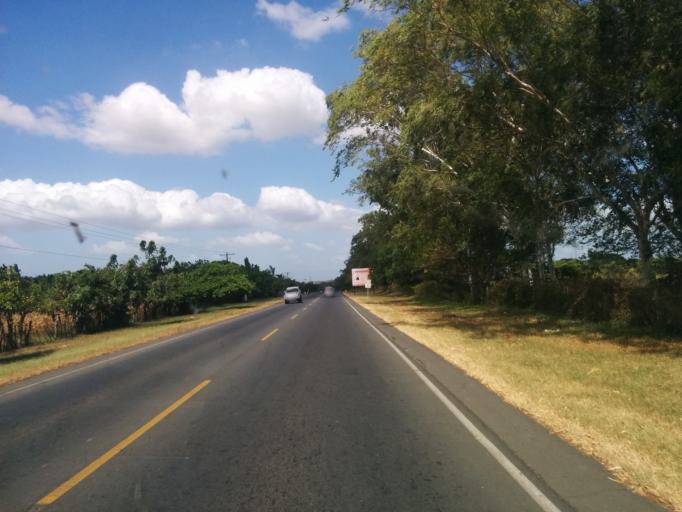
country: NI
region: Masaya
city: Nindiri
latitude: 12.0099
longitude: -86.1040
